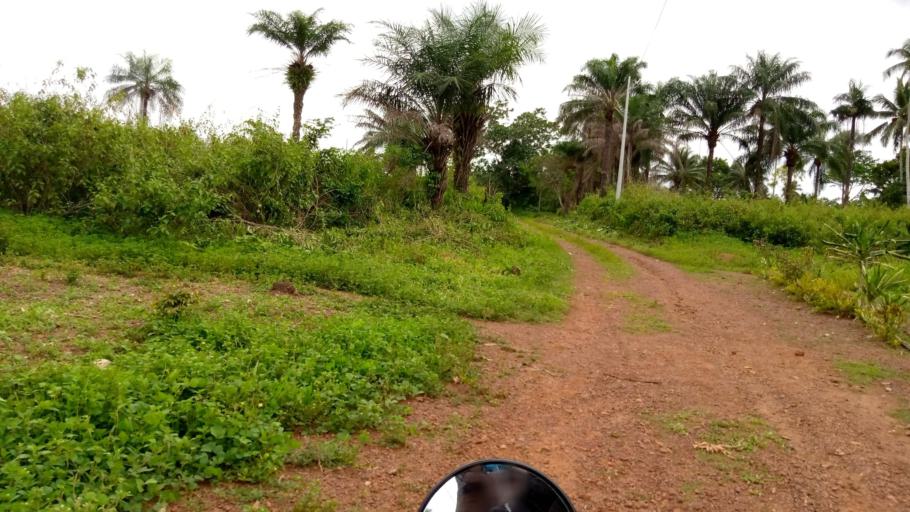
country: SL
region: Southern Province
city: Rotifunk
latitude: 8.1905
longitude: -12.5650
